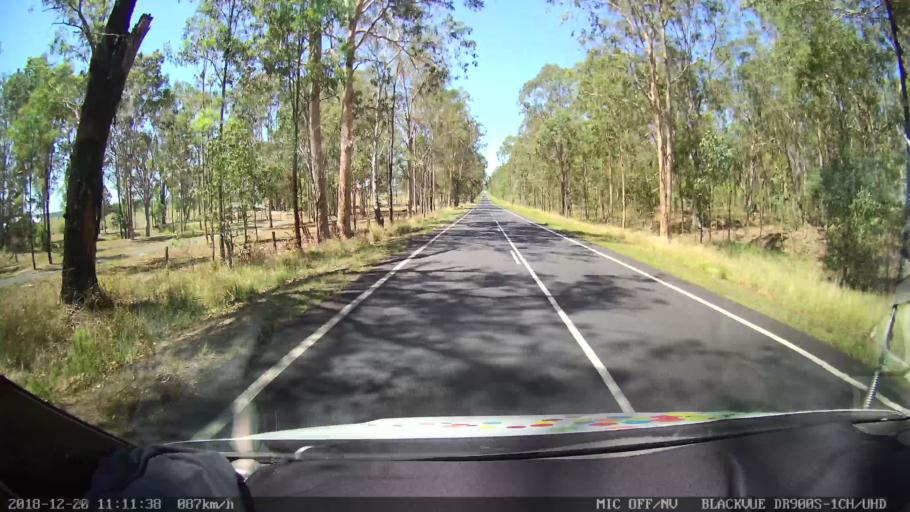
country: AU
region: New South Wales
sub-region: Richmond Valley
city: Casino
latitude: -28.9636
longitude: 153.0132
